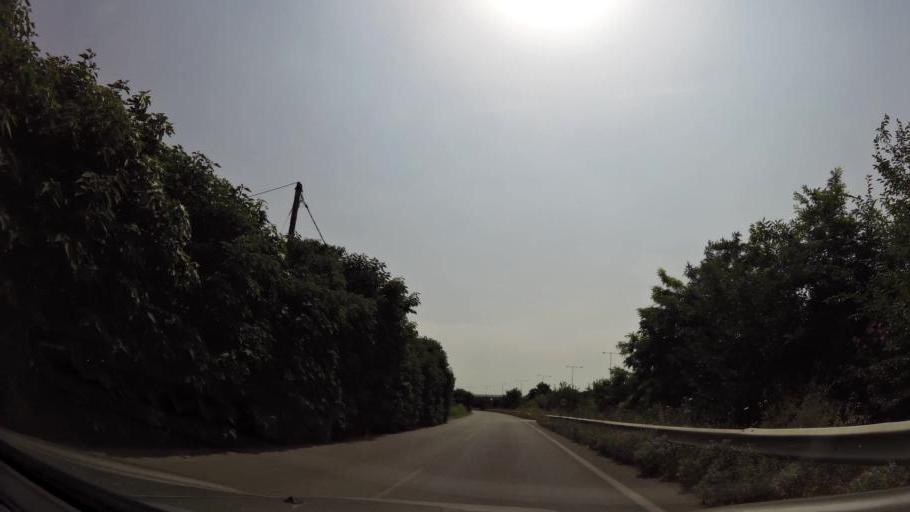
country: GR
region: Central Macedonia
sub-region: Nomos Thessalonikis
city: Nea Magnisia
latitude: 40.6902
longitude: 22.8380
